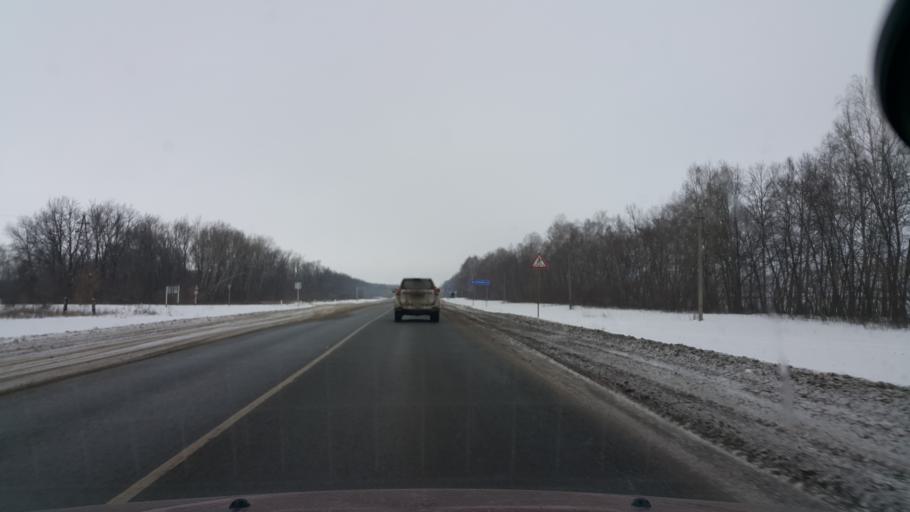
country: RU
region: Tambov
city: Bokino
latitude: 52.5868
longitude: 41.4488
